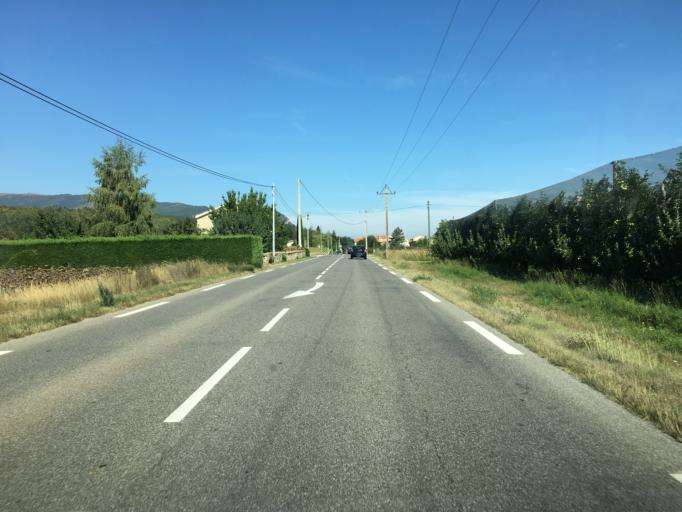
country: FR
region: Provence-Alpes-Cote d'Azur
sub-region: Departement des Hautes-Alpes
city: Laragne-Monteglin
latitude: 44.2773
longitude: 5.8515
